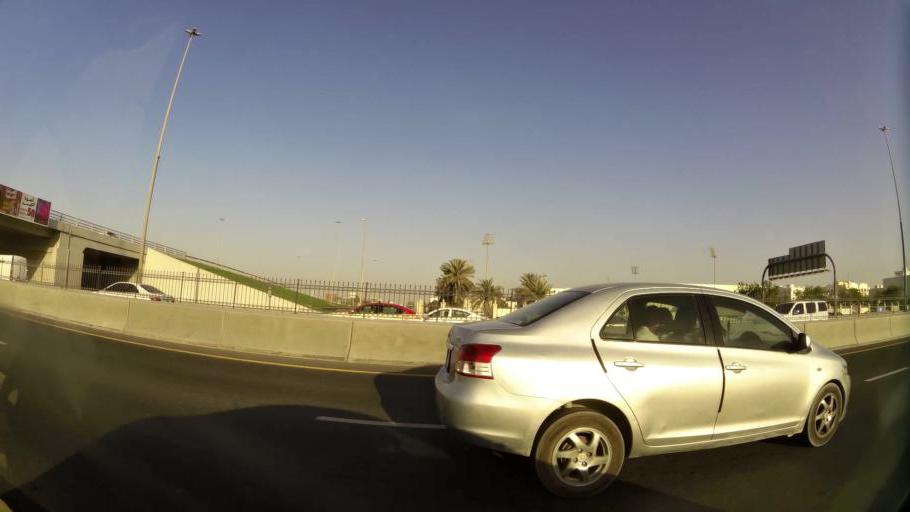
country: AE
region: Ash Shariqah
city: Sharjah
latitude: 25.3156
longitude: 55.4510
